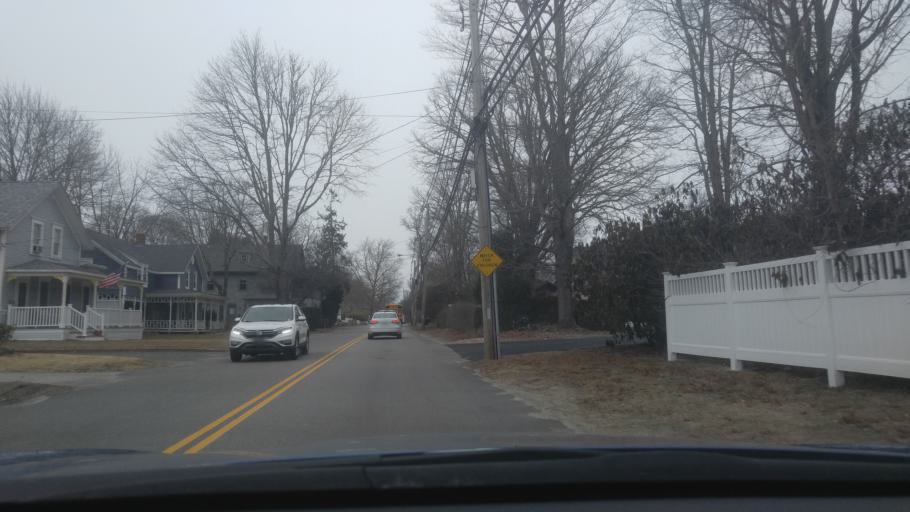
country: US
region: Rhode Island
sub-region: Washington County
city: Wakefield-Peacedale
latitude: 41.4366
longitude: -71.4948
